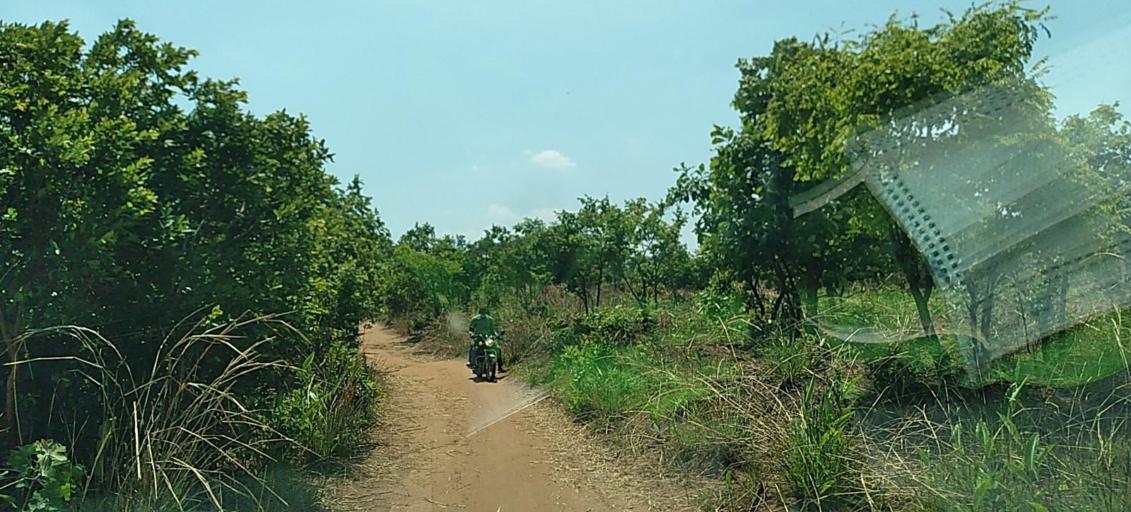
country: CD
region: Katanga
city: Kolwezi
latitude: -11.2906
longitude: 25.2049
